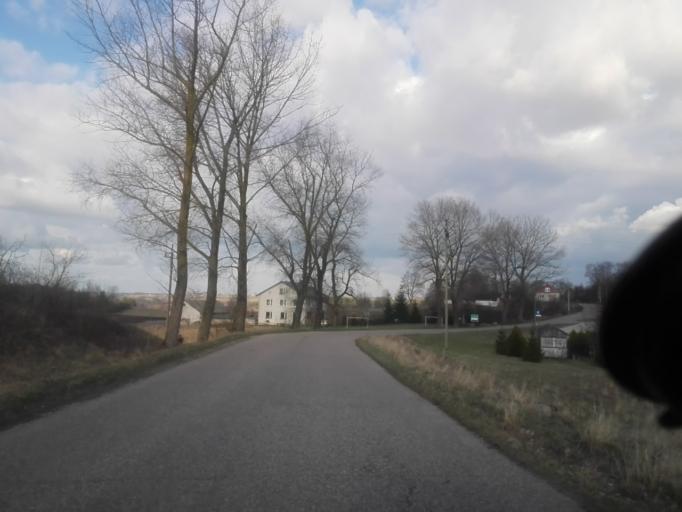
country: PL
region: Podlasie
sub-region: Suwalki
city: Suwalki
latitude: 54.2184
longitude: 22.8738
